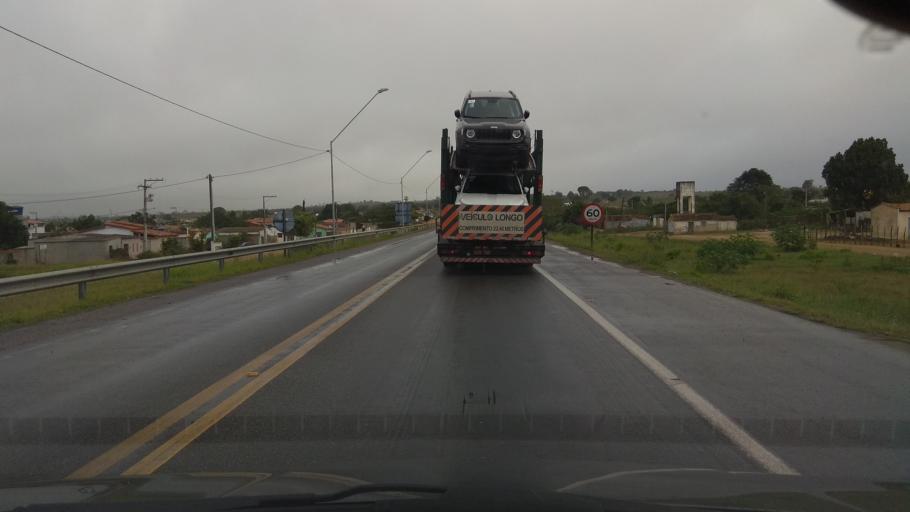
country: BR
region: Bahia
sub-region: Santa Ines
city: Santa Ines
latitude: -13.0765
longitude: -39.9616
